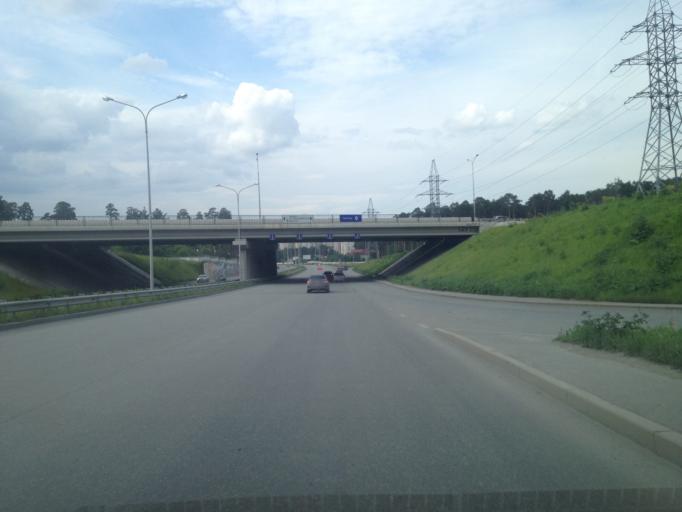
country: RU
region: Sverdlovsk
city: Sovkhoznyy
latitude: 56.7891
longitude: 60.5980
